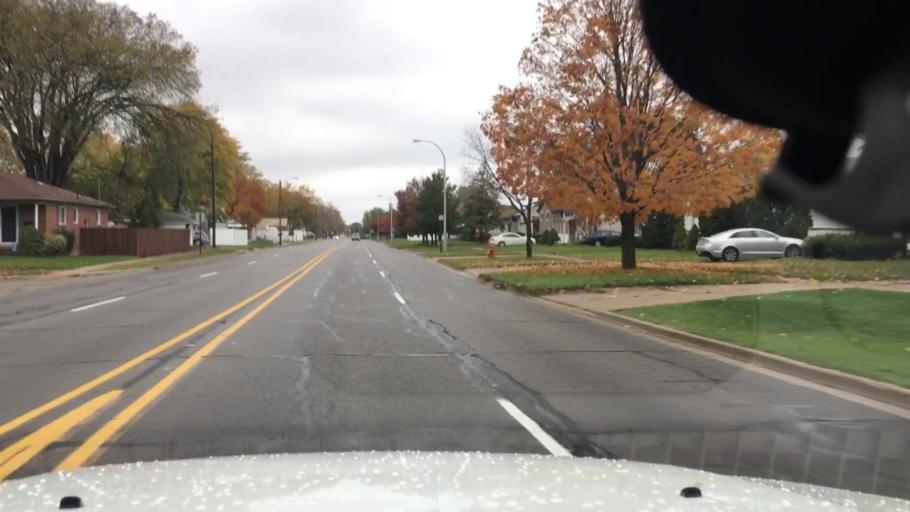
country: US
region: Michigan
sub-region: Oakland County
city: Clawson
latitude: 42.5211
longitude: -83.1257
